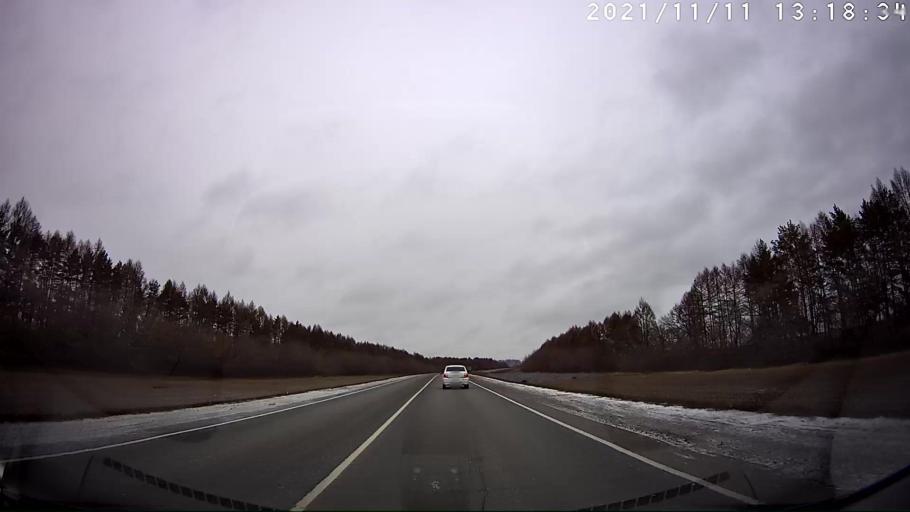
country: RU
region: Chuvashia
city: Komsomol'skoye
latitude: 55.1676
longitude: 47.5428
